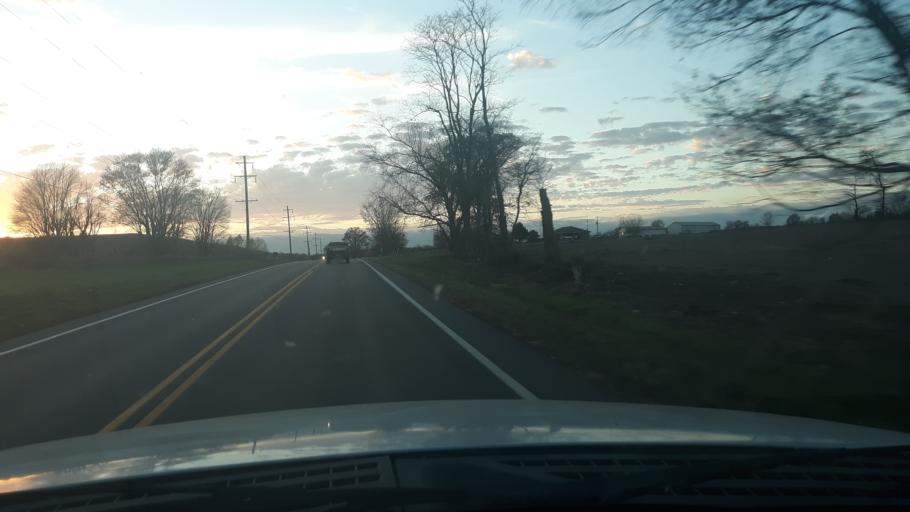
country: US
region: Illinois
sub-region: Saline County
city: Harrisburg
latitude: 37.8347
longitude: -88.5661
